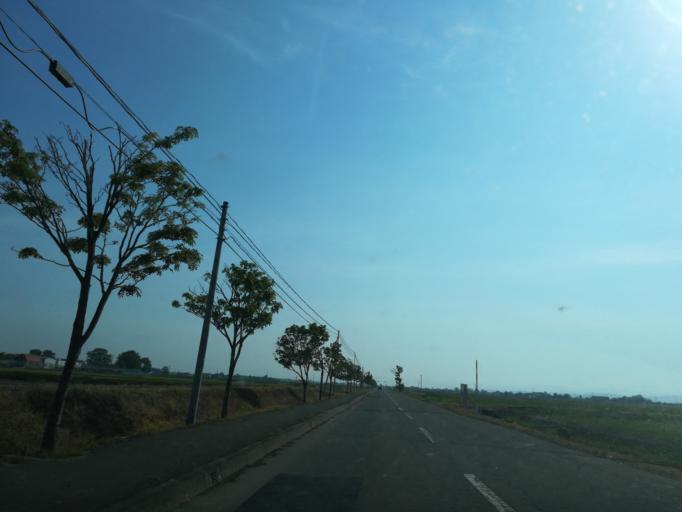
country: JP
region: Hokkaido
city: Iwamizawa
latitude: 43.1563
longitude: 141.6776
